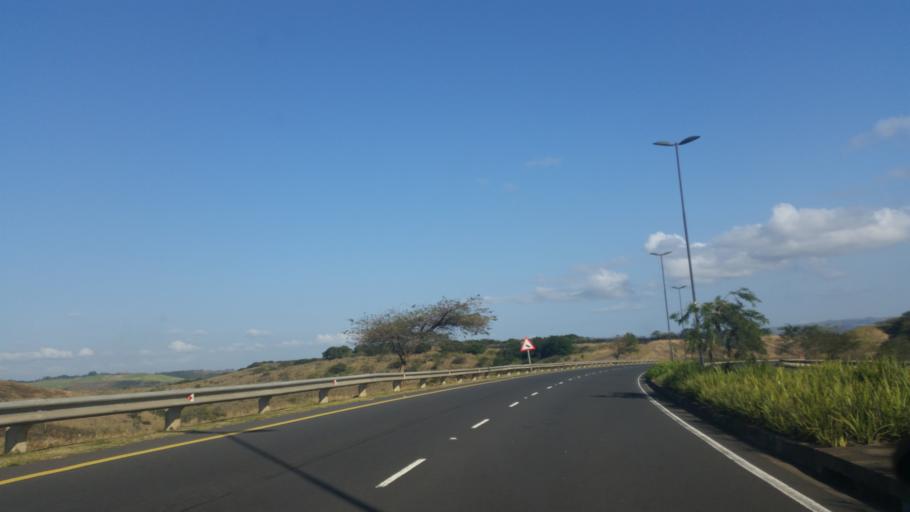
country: ZA
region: KwaZulu-Natal
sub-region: iLembe District Municipality
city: Ballitoville
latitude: -29.6281
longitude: 31.1078
